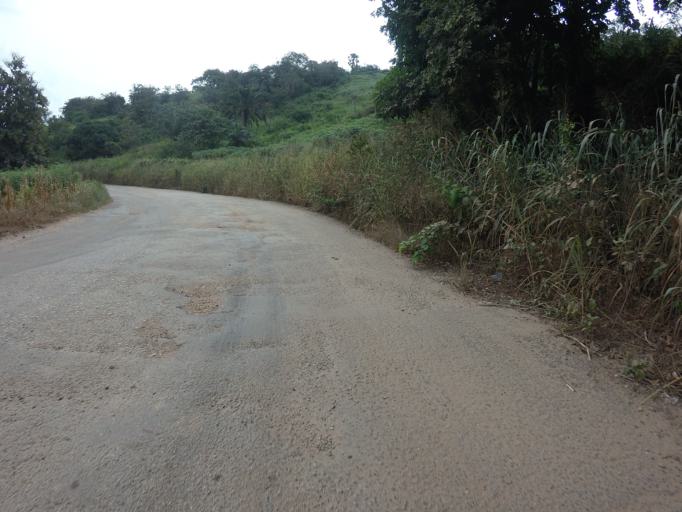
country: GH
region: Volta
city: Ho
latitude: 6.6871
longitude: 0.3460
